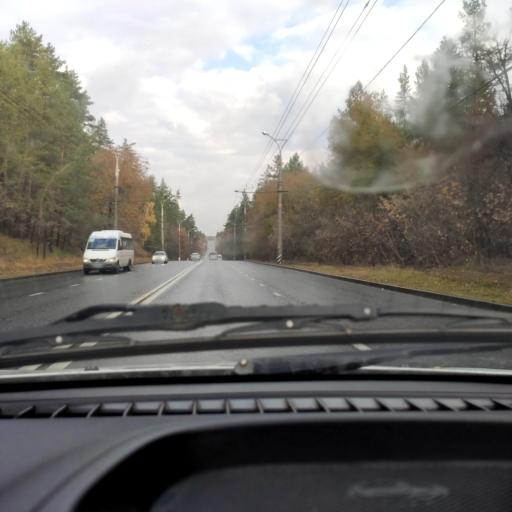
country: RU
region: Samara
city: Zhigulevsk
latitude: 53.4942
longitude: 49.4630
